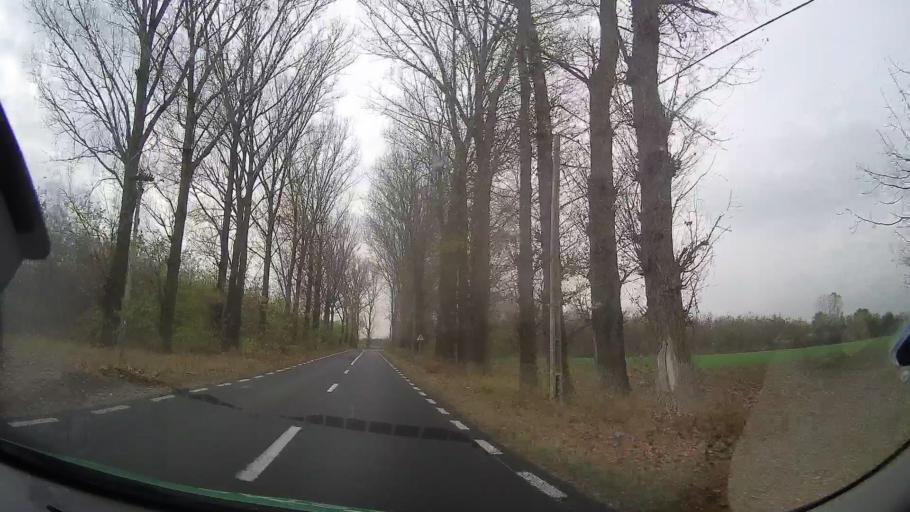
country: RO
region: Ilfov
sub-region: Comuna Nuci
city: Nuci
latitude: 44.7220
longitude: 26.2896
